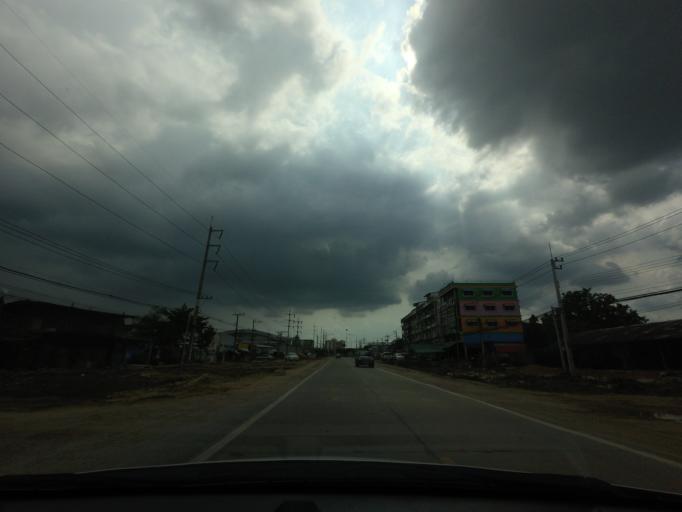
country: TH
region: Nakhon Pathom
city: Sam Phran
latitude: 13.7483
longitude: 100.2301
